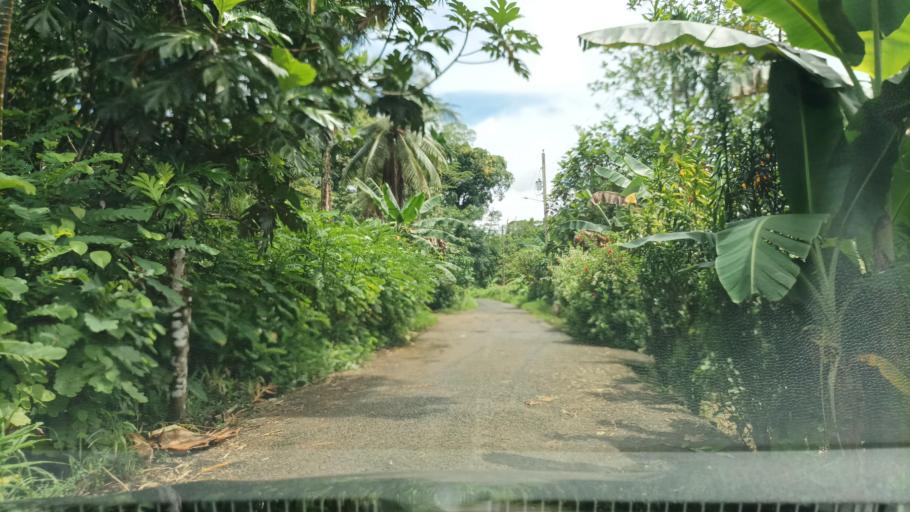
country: FM
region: Pohnpei
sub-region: Kolonia Municipality
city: Kolonia
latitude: 6.9678
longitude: 158.2241
